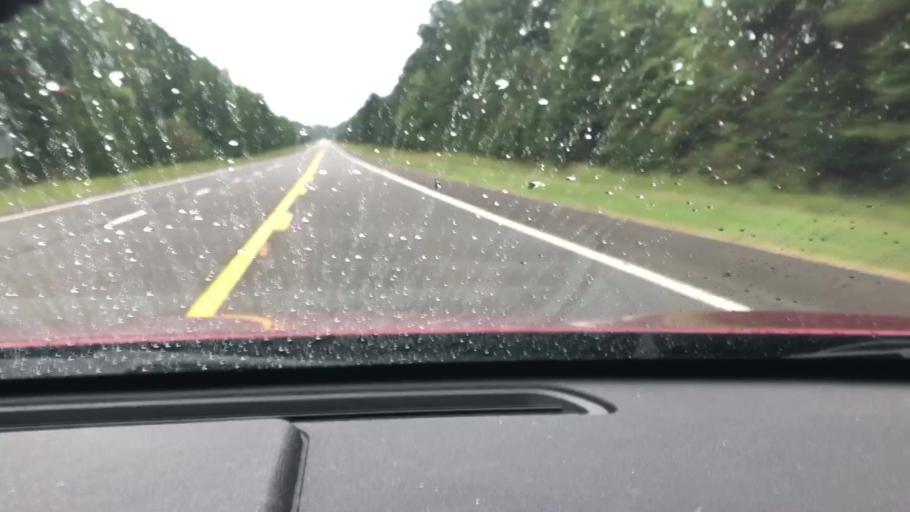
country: US
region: Arkansas
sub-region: Columbia County
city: Waldo
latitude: 33.3067
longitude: -93.2753
